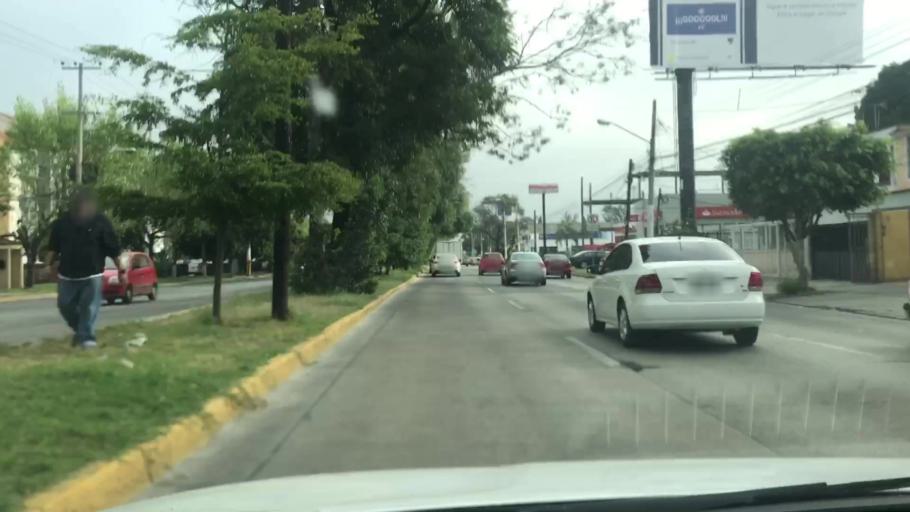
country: MX
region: Jalisco
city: Guadalajara
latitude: 20.6327
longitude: -103.4279
